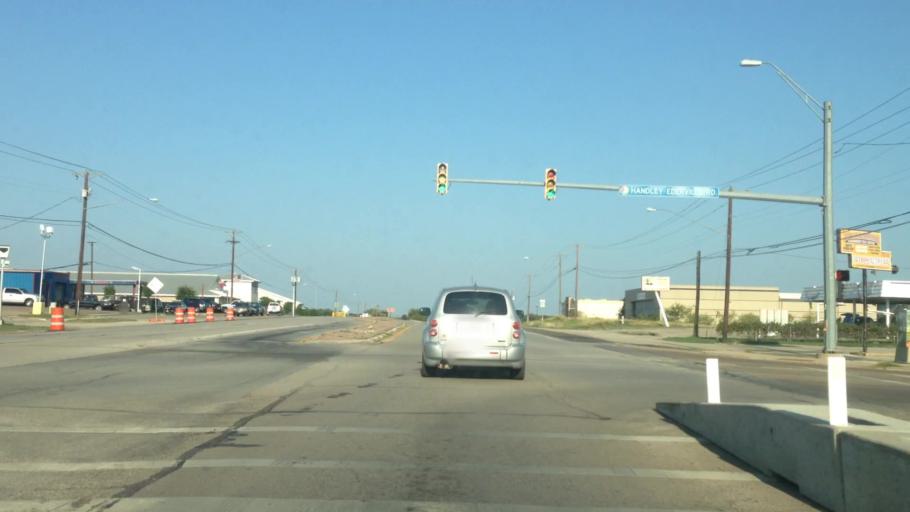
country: US
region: Texas
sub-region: Tarrant County
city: Richland Hills
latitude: 32.8090
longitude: -97.2213
